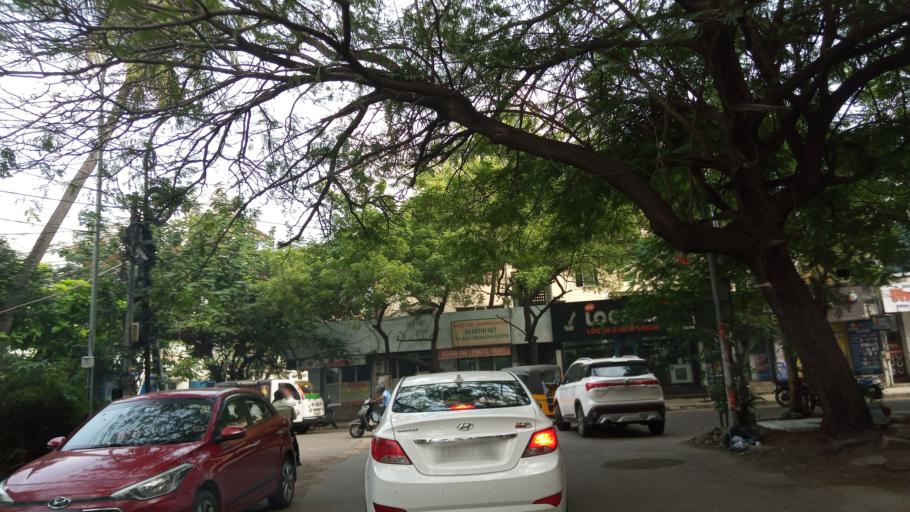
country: IN
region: Tamil Nadu
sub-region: Kancheepuram
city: Alandur
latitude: 13.0373
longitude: 80.2162
